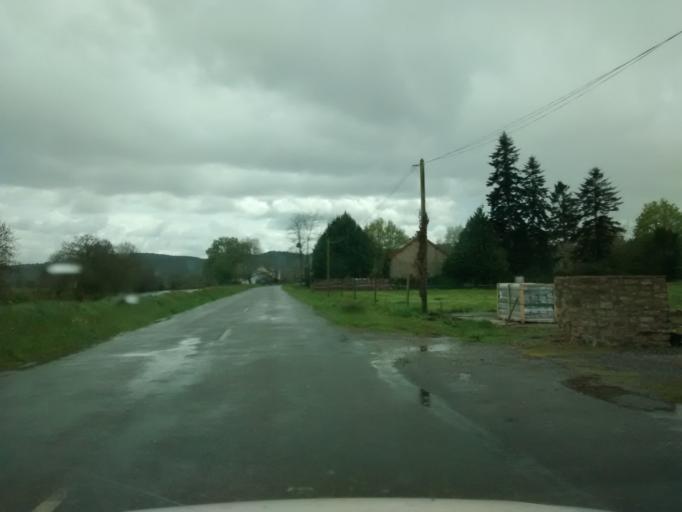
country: FR
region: Brittany
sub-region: Departement du Morbihan
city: Pleucadeuc
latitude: 47.7631
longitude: -2.3177
